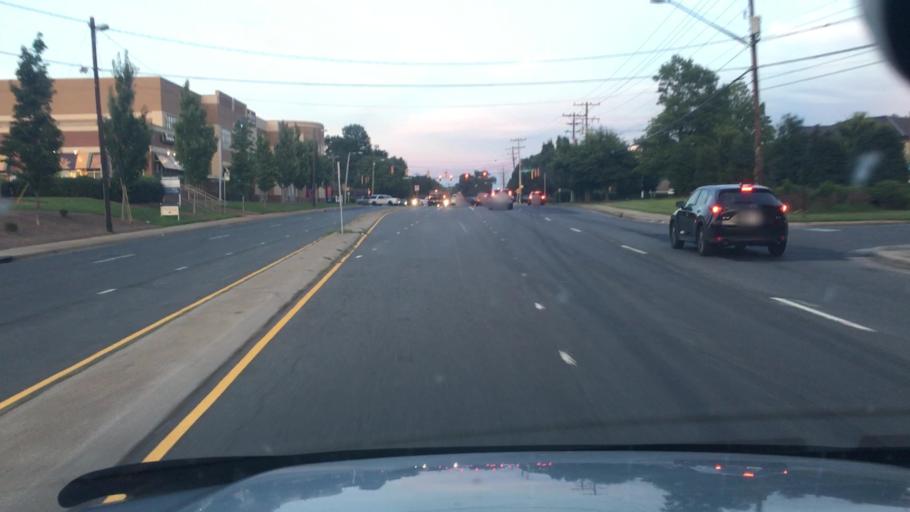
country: US
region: North Carolina
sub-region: Mecklenburg County
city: Pineville
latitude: 35.0877
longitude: -80.8469
